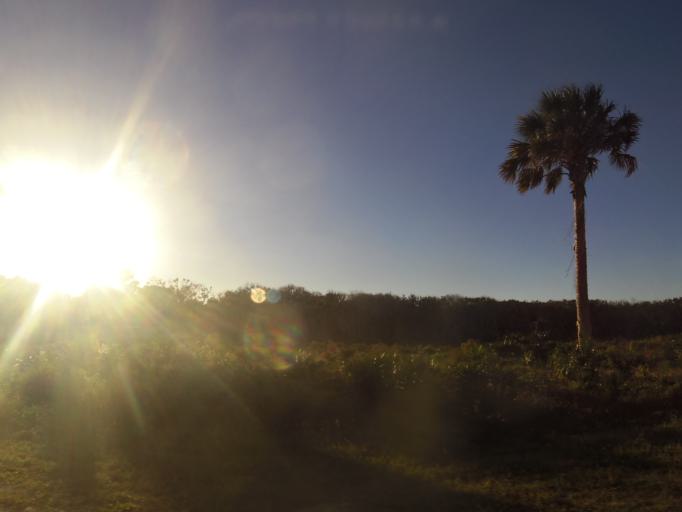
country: US
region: Florida
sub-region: Flagler County
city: Palm Coast
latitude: 29.6324
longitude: -81.2047
